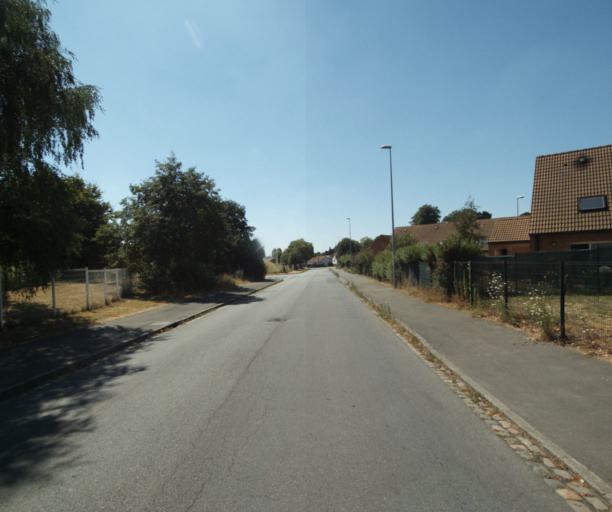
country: BE
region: Wallonia
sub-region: Province du Hainaut
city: Mouscron
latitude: 50.7322
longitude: 3.1882
